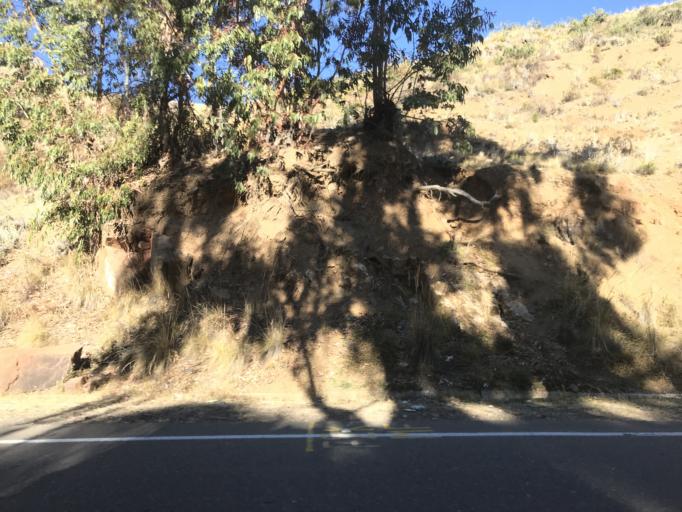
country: BO
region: La Paz
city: San Pedro
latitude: -16.2238
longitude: -68.8558
